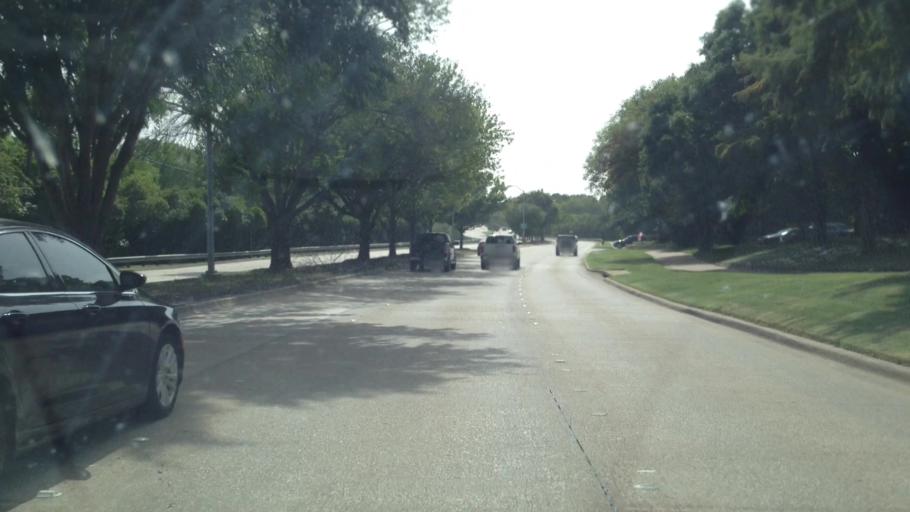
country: US
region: Texas
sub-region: Dallas County
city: Addison
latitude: 33.0277
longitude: -96.8089
